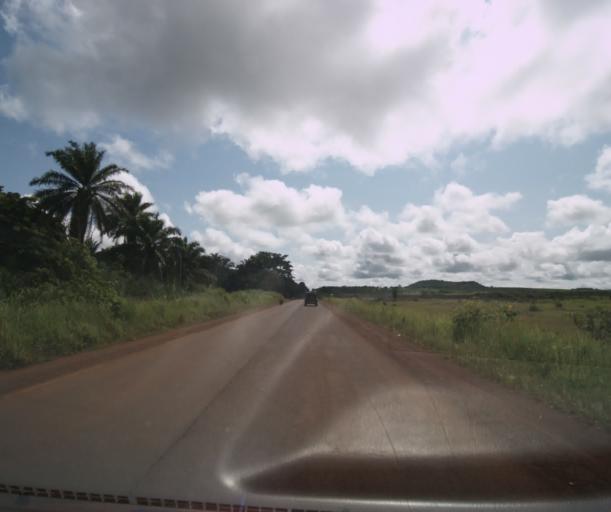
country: CM
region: West
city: Foumban
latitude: 5.6561
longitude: 10.7684
